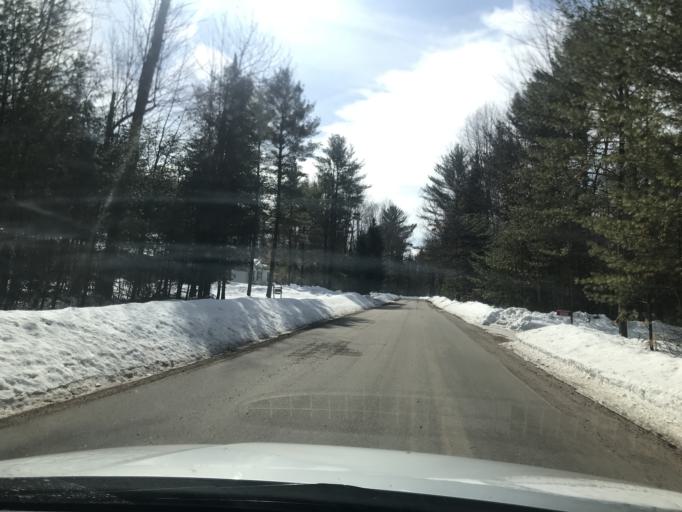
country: US
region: Wisconsin
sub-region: Menominee County
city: Legend Lake
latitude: 45.1194
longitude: -88.4463
